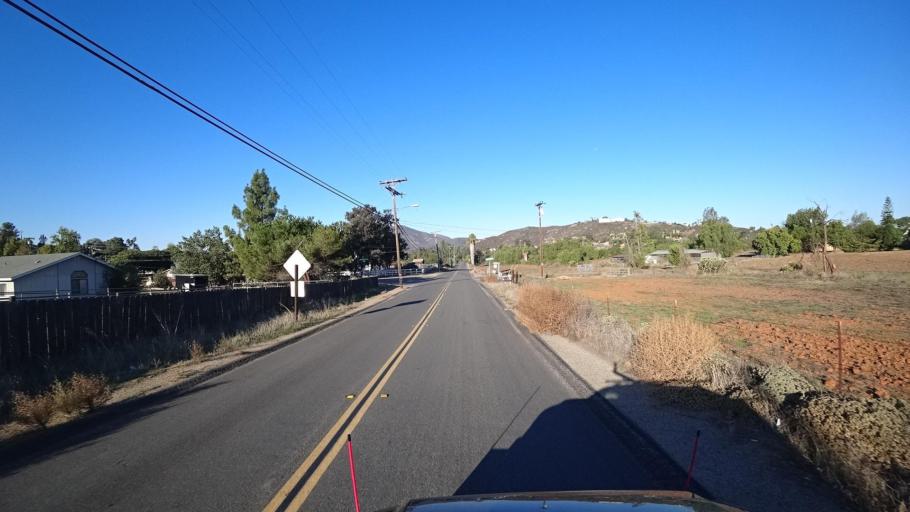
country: US
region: California
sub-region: San Diego County
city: Jamul
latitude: 32.7066
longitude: -116.8820
